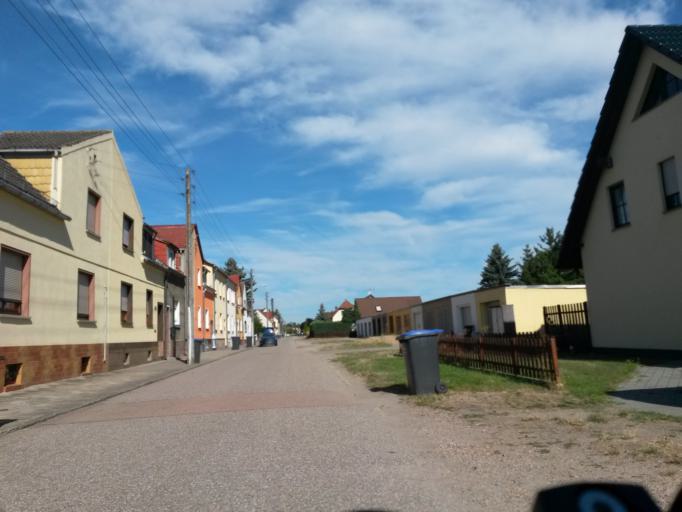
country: DE
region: Saxony-Anhalt
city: Coswig
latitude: 51.8750
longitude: 12.4758
